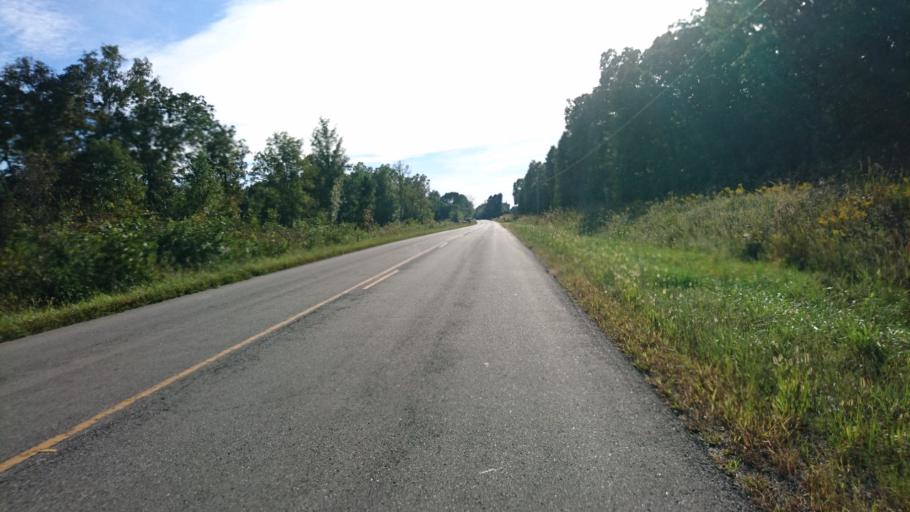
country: US
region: Missouri
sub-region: Crawford County
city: Cuba
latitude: 38.1066
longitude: -91.3419
